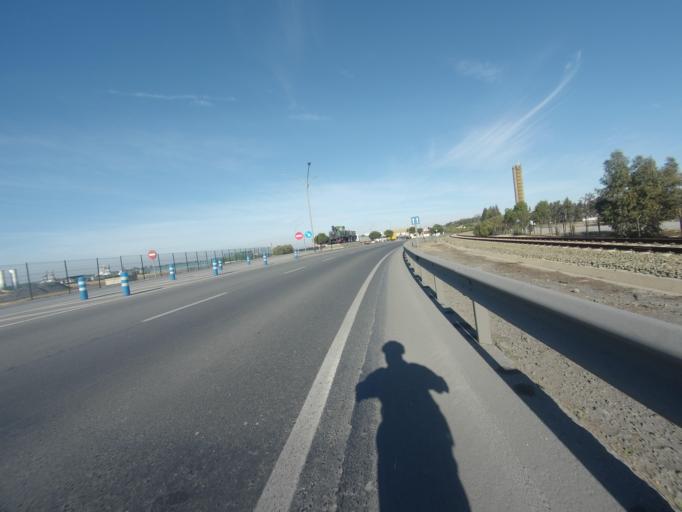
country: ES
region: Andalusia
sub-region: Provincia de Huelva
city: Punta Umbria
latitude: 37.1981
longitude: -6.9342
